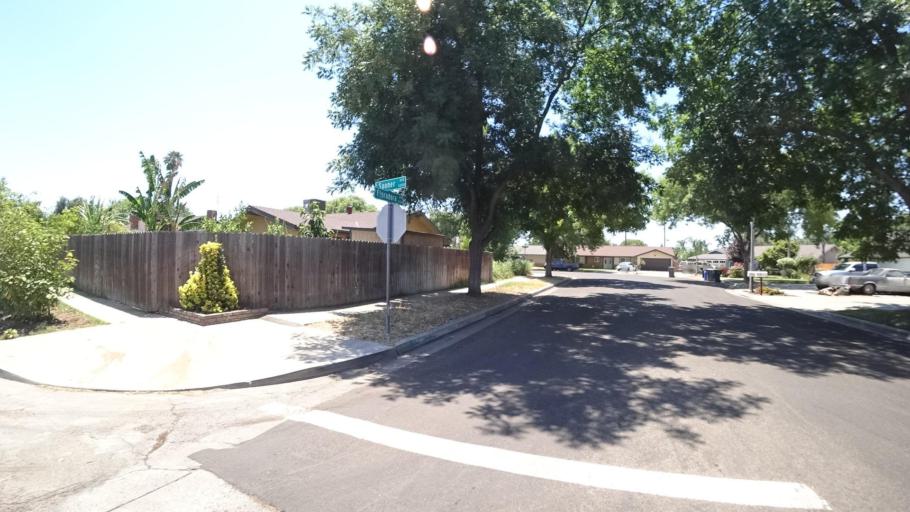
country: US
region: California
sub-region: Fresno County
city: Sunnyside
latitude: 36.7613
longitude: -119.7244
